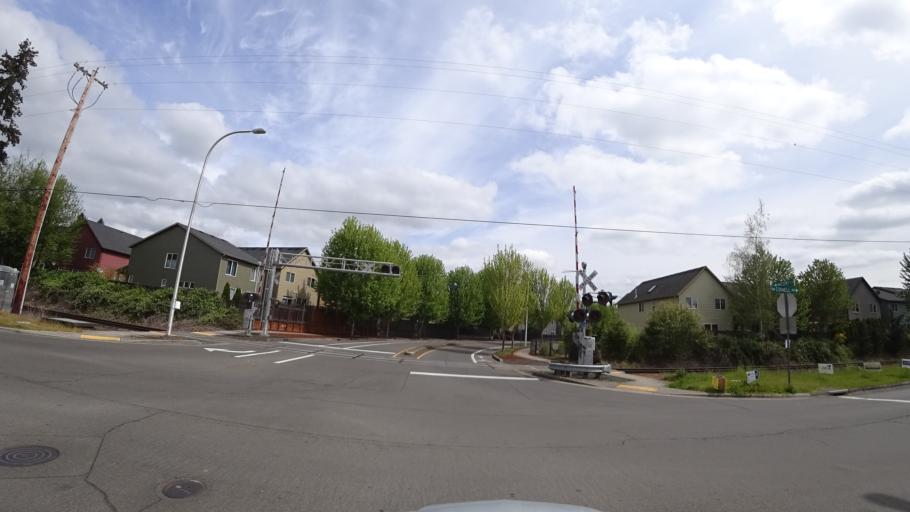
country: US
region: Oregon
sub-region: Washington County
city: Hillsboro
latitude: 45.5390
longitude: -122.9978
